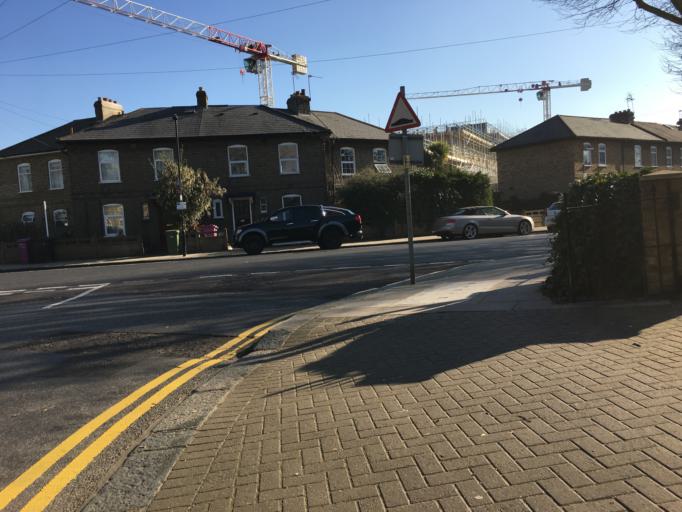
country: GB
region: England
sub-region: Greater London
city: Poplar
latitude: 51.4891
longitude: -0.0164
